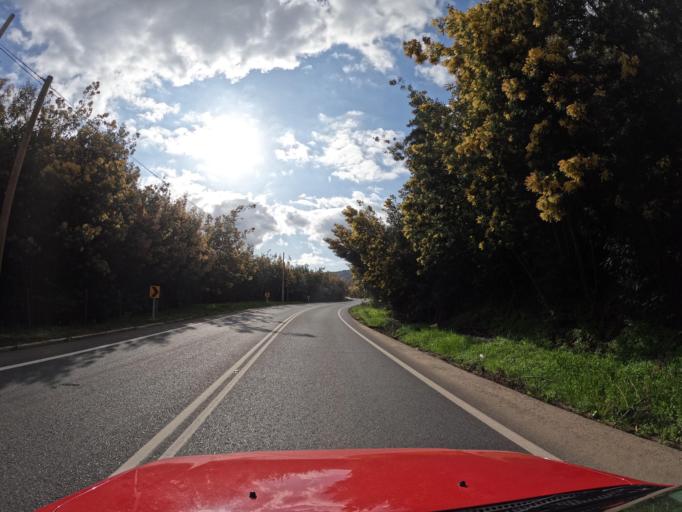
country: CL
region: Maule
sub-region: Provincia de Talca
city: Constitucion
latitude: -35.5447
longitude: -72.1511
